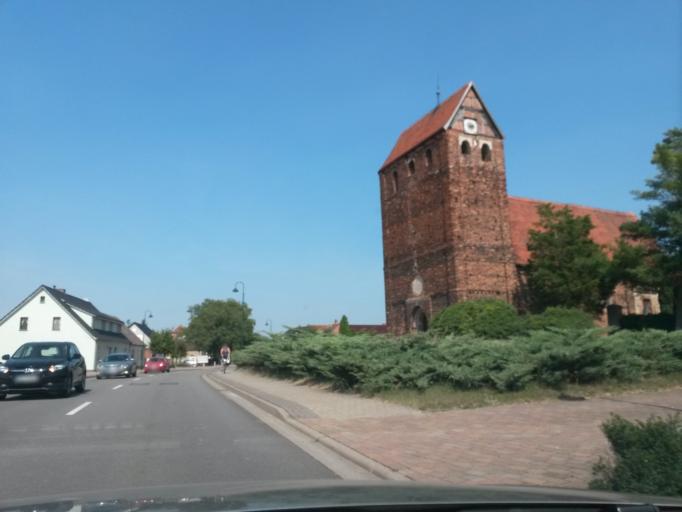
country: DE
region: Saxony-Anhalt
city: Jerichow
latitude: 52.5384
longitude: 12.0156
